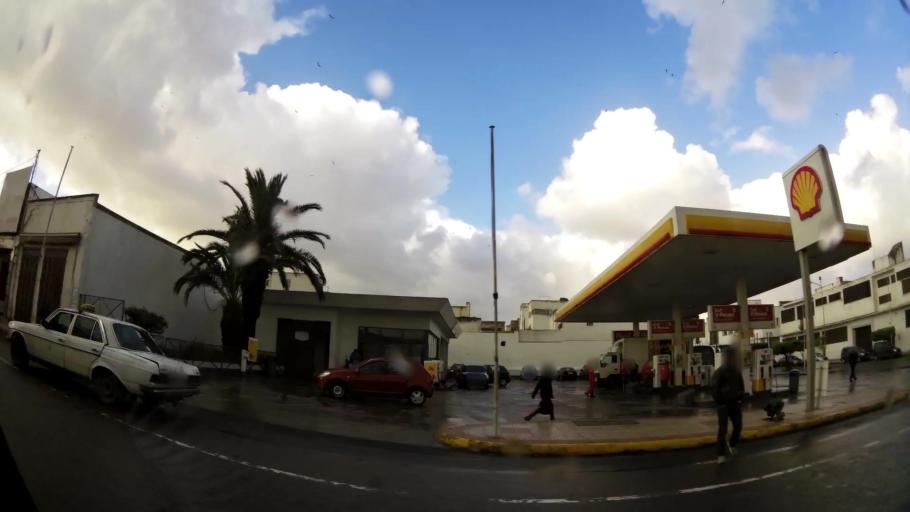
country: MA
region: Grand Casablanca
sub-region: Casablanca
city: Casablanca
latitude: 33.5829
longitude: -7.6037
